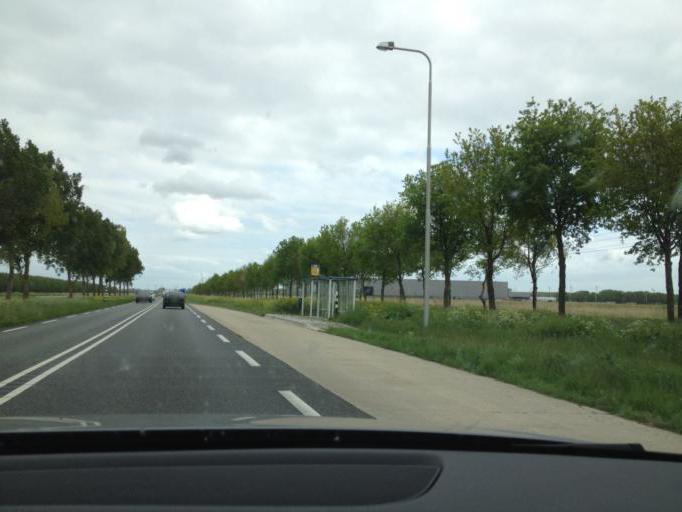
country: NL
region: North Holland
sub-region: Gemeente Huizen
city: Huizen
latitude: 52.3215
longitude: 5.3140
